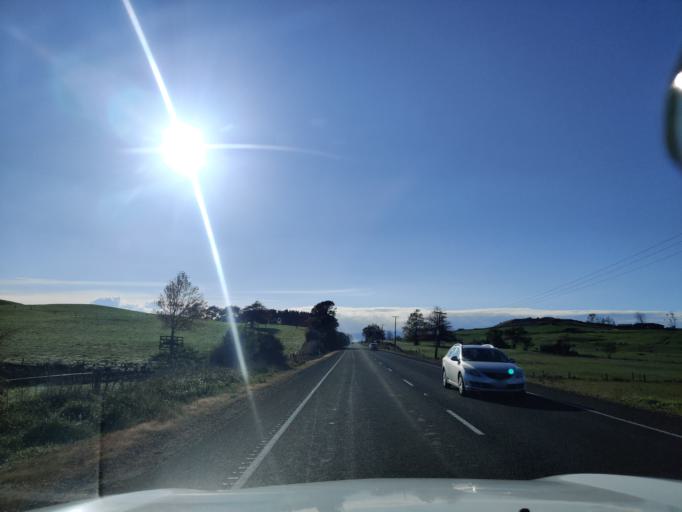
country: NZ
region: Waikato
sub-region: Hauraki District
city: Ngatea
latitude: -37.2858
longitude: 175.3931
